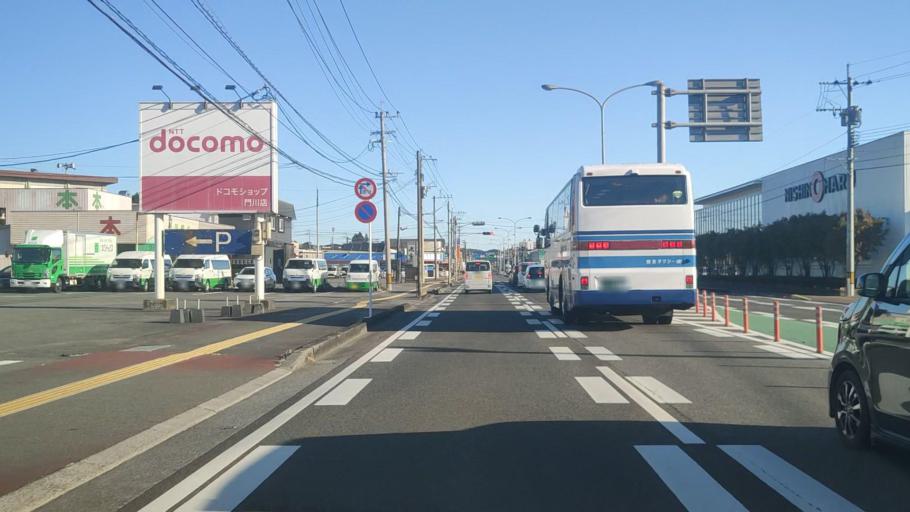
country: JP
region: Miyazaki
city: Nobeoka
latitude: 32.4684
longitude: 131.6488
